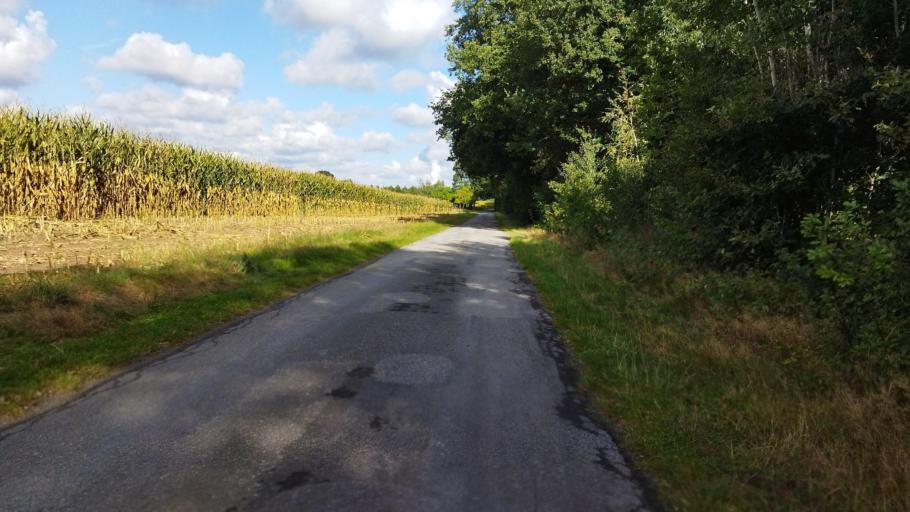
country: DE
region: Lower Saxony
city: Salzbergen
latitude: 52.3622
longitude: 7.3347
